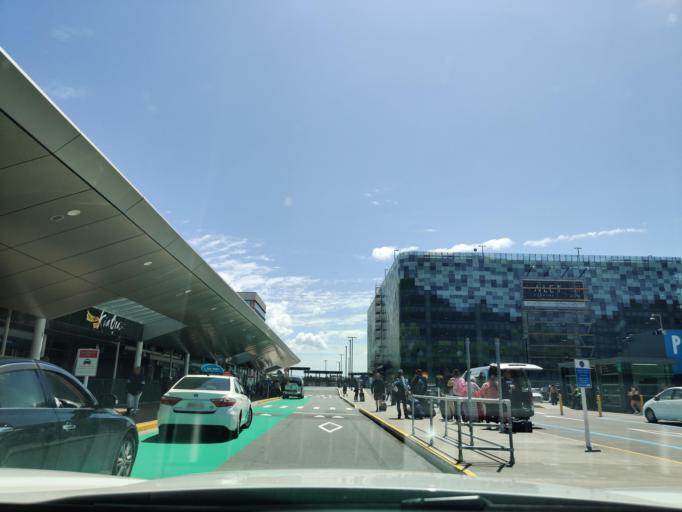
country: NZ
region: Wellington
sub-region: Wellington City
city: Wellington
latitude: -41.3293
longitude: 174.8122
